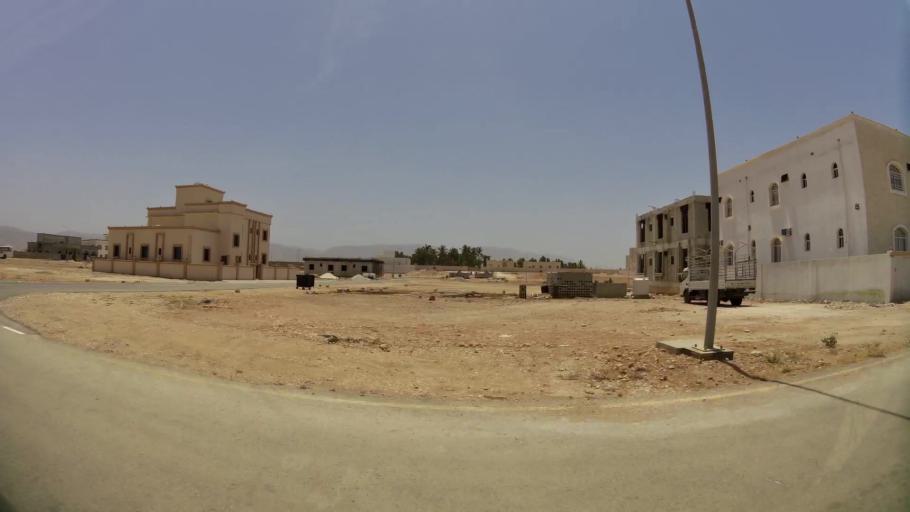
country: OM
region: Zufar
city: Salalah
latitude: 17.0849
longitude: 54.1841
